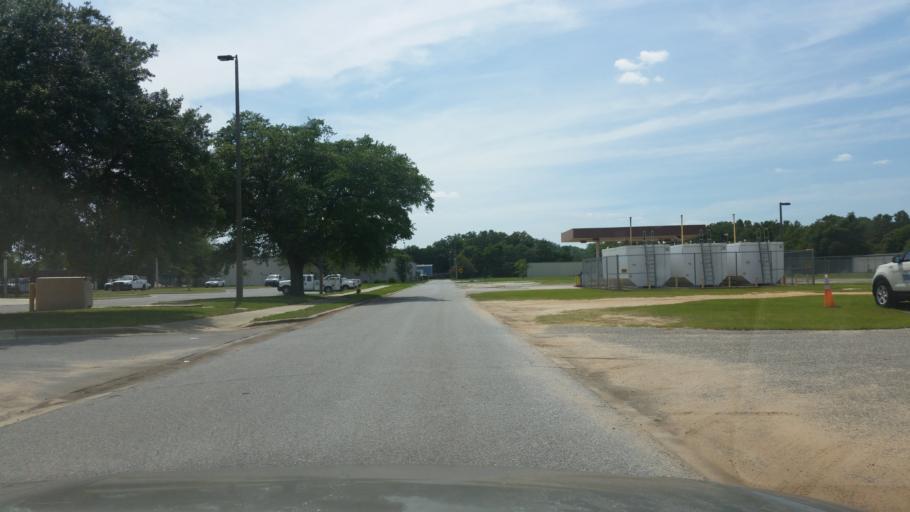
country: US
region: Florida
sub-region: Escambia County
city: Ferry Pass
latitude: 30.5306
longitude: -87.1989
